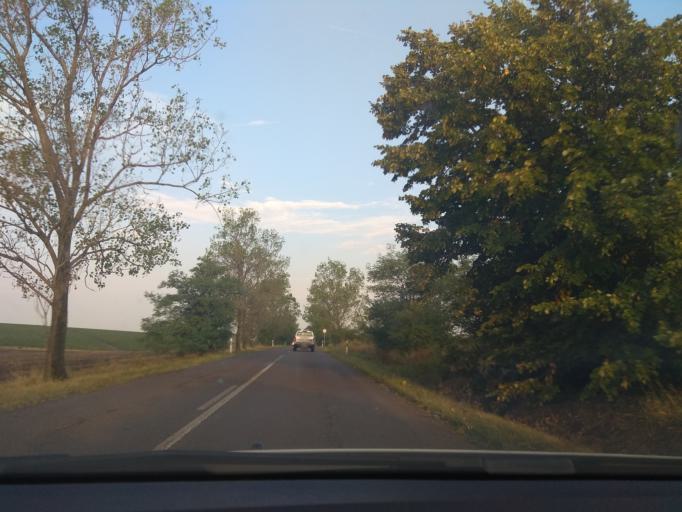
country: HU
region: Heves
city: Andornaktalya
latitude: 47.8303
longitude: 20.4519
